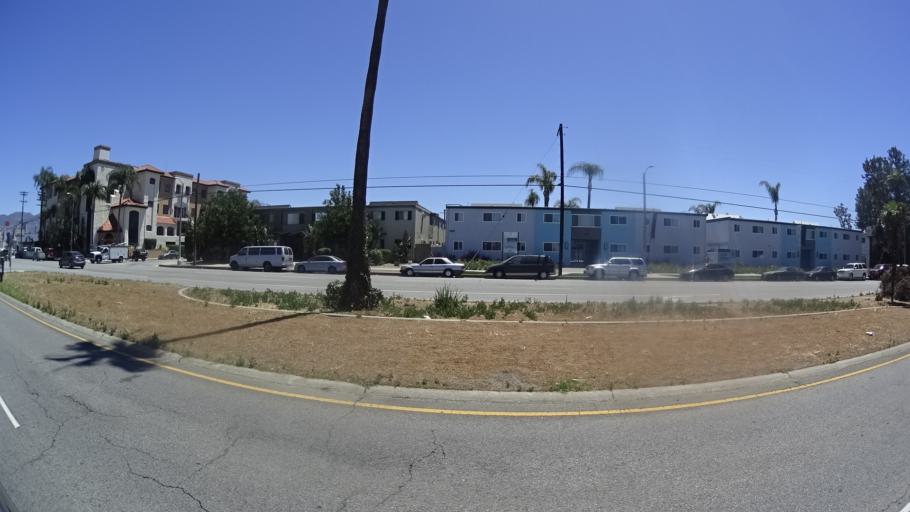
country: US
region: California
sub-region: Los Angeles County
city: San Fernando
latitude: 34.2551
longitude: -118.4675
